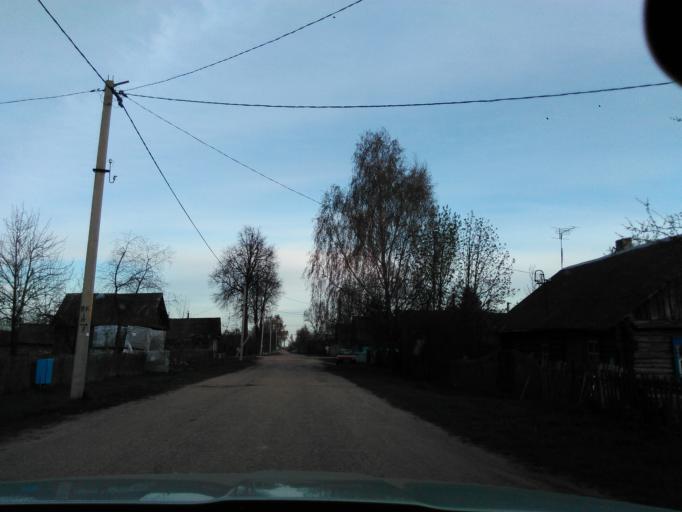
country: BY
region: Vitebsk
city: Chashniki
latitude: 54.8531
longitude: 29.1720
